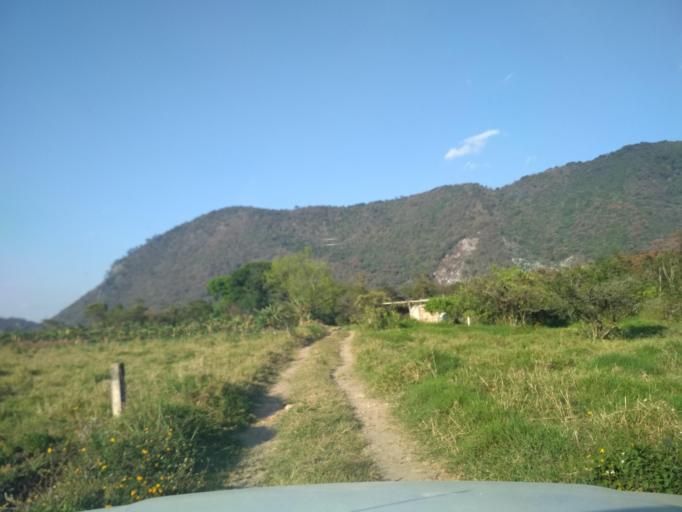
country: MX
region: Veracruz
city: Jalapilla
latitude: 18.8175
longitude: -97.0732
